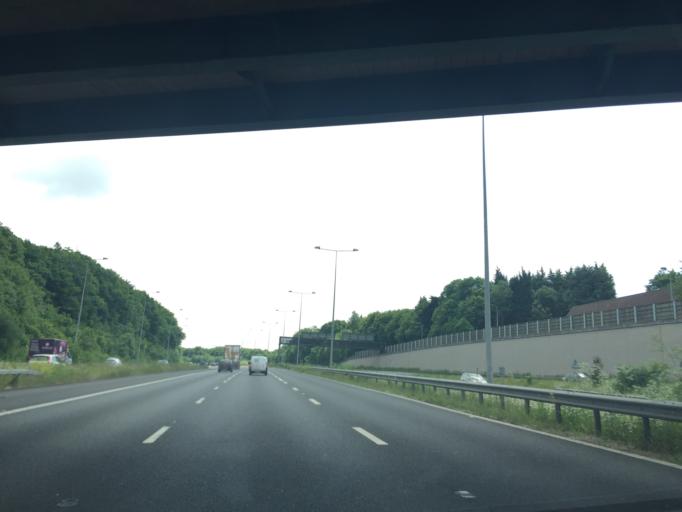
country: GB
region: England
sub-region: Kent
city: Boxley
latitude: 51.3336
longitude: 0.5115
